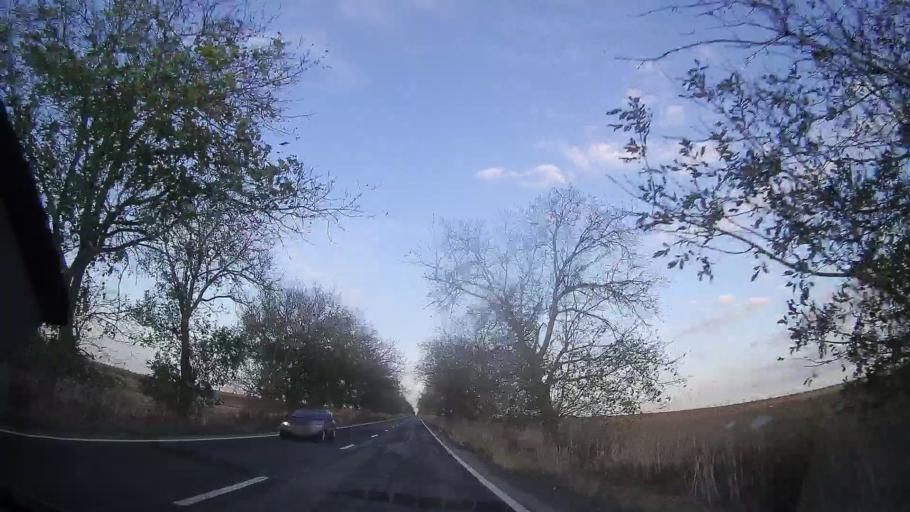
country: RO
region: Constanta
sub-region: Comuna Chirnogeni
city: Chirnogeni
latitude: 43.8588
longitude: 28.2550
